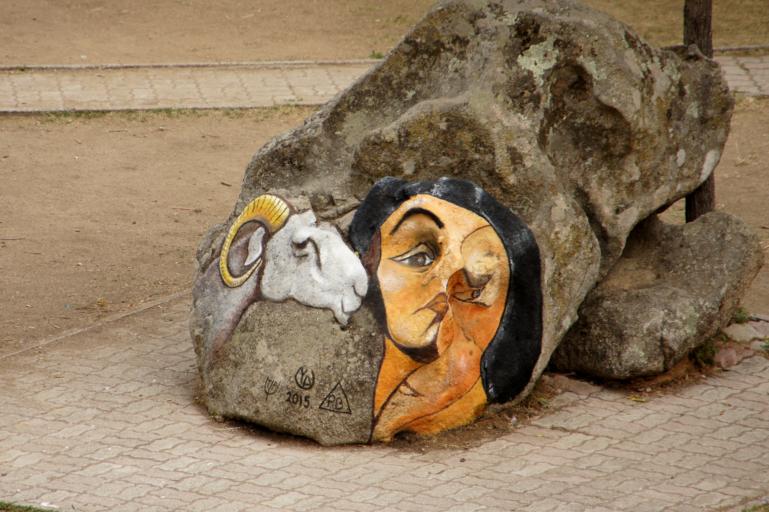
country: IT
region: Sardinia
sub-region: Provincia di Nuoro
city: Orgosolo
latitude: 40.2040
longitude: 9.3539
